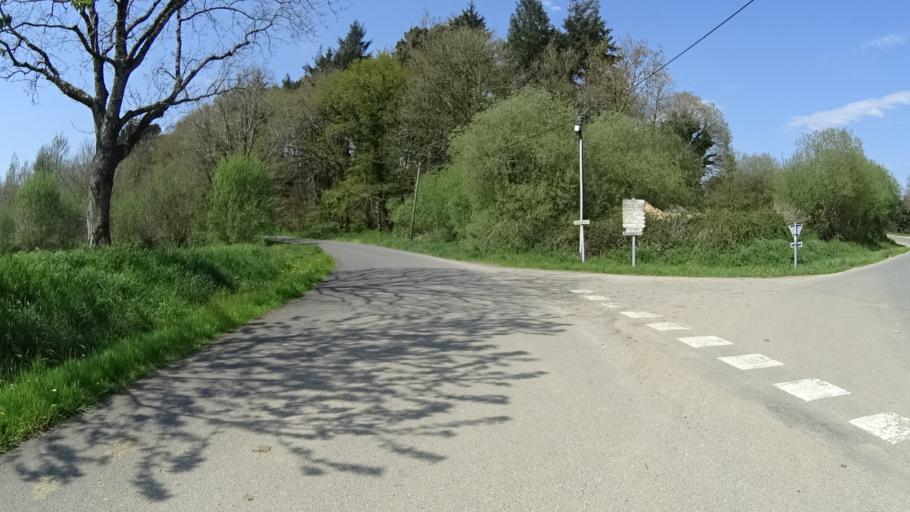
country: FR
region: Brittany
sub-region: Departement du Finistere
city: Sizun
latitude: 48.4124
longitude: -4.0862
